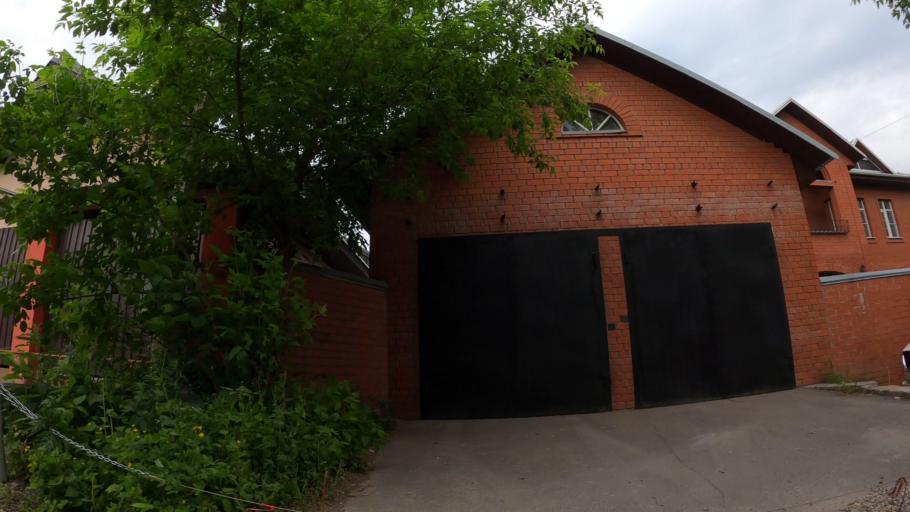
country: RU
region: Moskovskaya
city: Ivanteyevka
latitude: 55.9669
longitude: 37.9204
